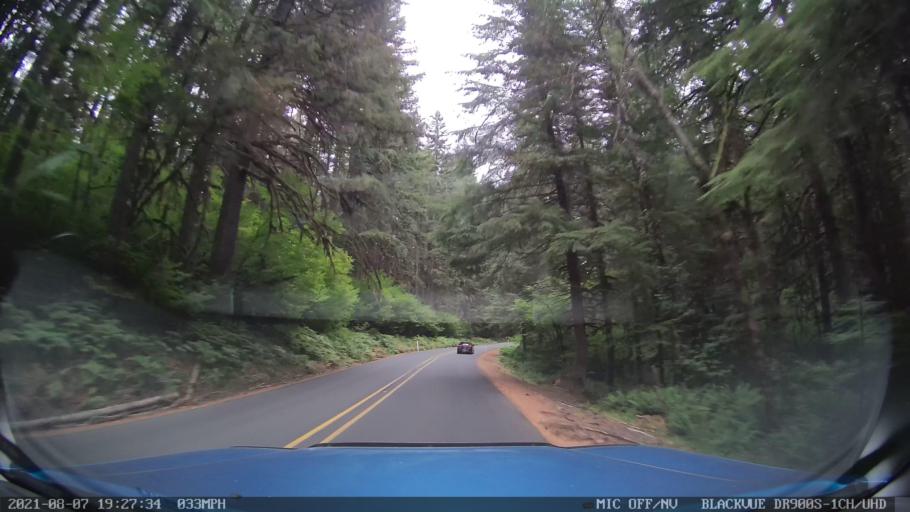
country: US
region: Oregon
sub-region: Linn County
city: Lyons
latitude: 44.8785
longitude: -122.6445
